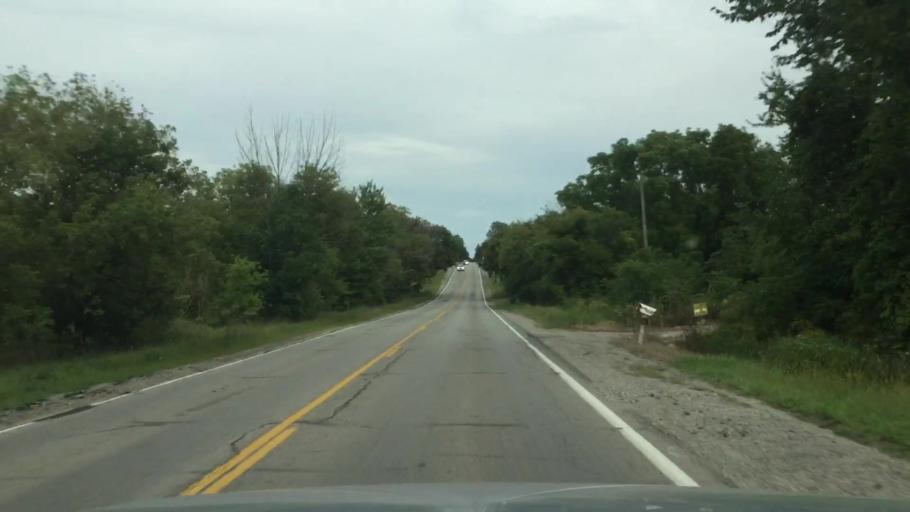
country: US
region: Michigan
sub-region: Genesee County
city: Lake Fenton
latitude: 42.8854
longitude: -83.7223
